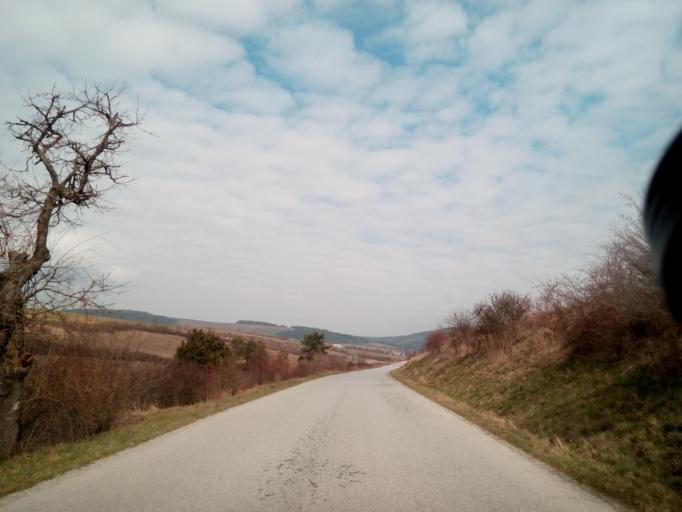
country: SK
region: Presovsky
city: Sabinov
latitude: 49.0291
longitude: 21.0194
